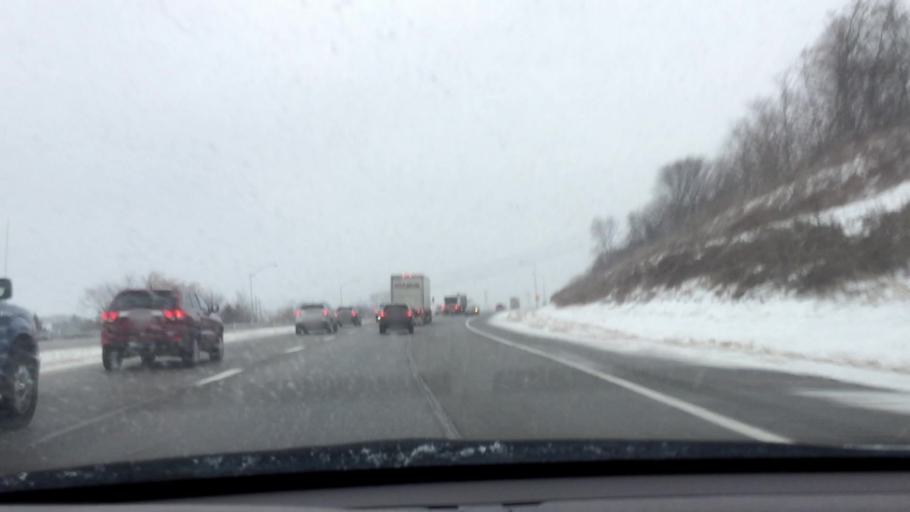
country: US
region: Pennsylvania
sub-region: Washington County
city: Muse
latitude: 40.2905
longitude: -80.1696
